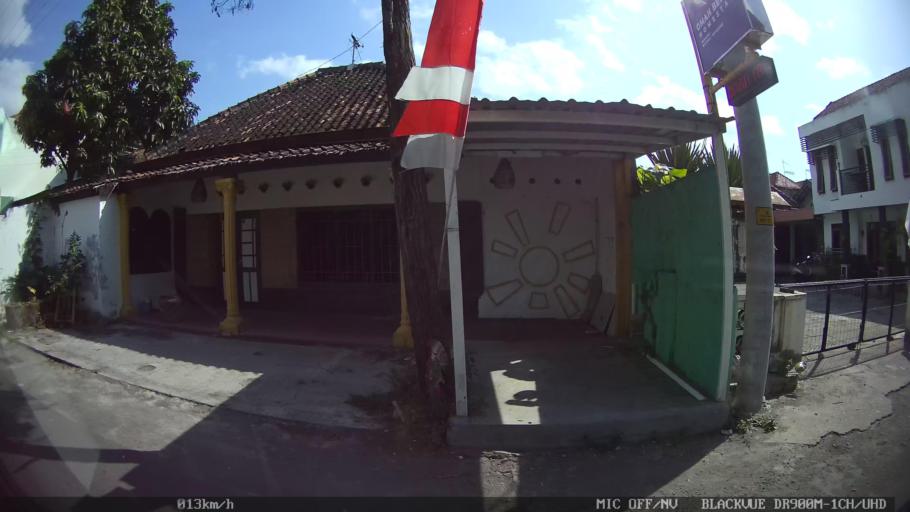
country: ID
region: Daerah Istimewa Yogyakarta
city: Yogyakarta
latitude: -7.8200
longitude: 110.3703
